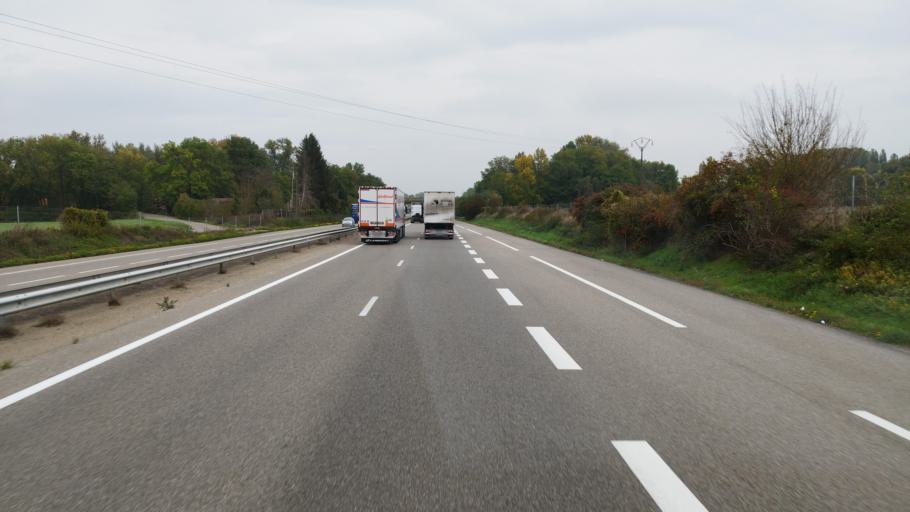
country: FR
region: Alsace
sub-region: Departement du Bas-Rhin
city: Soufflenheim
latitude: 48.8262
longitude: 8.0029
